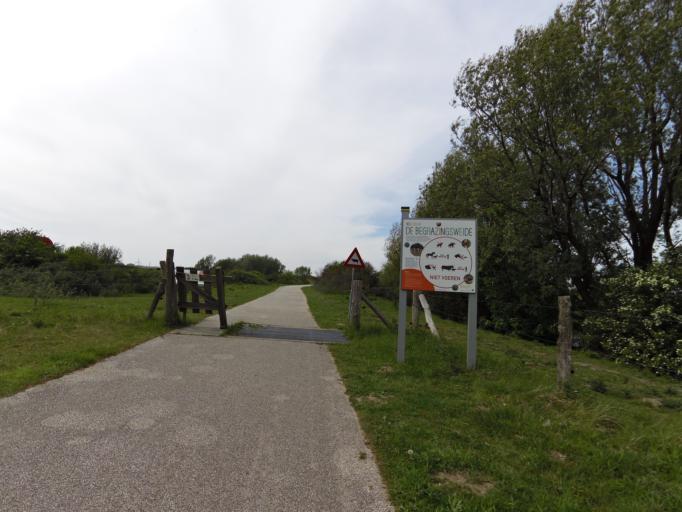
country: NL
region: South Holland
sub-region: Gemeente Maassluis
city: Maassluis
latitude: 51.9256
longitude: 4.2183
